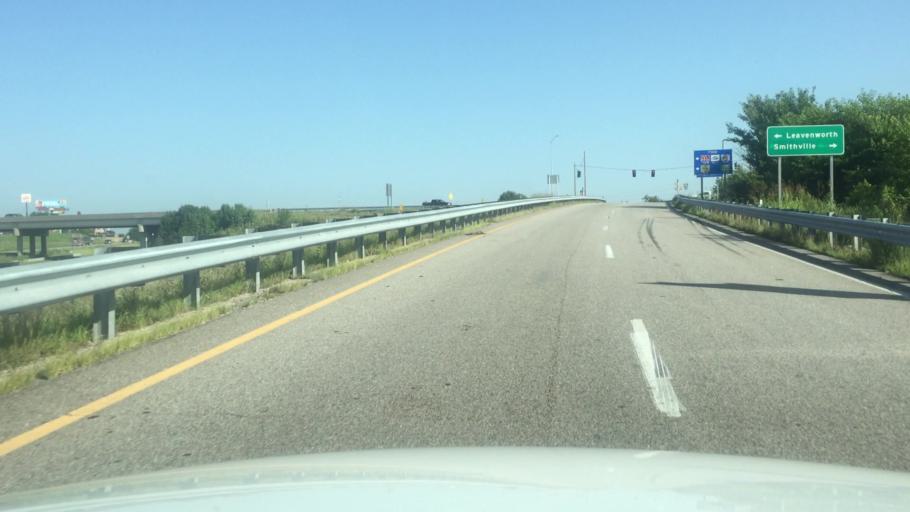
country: US
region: Missouri
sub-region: Platte County
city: Platte City
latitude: 39.3526
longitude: -94.7599
